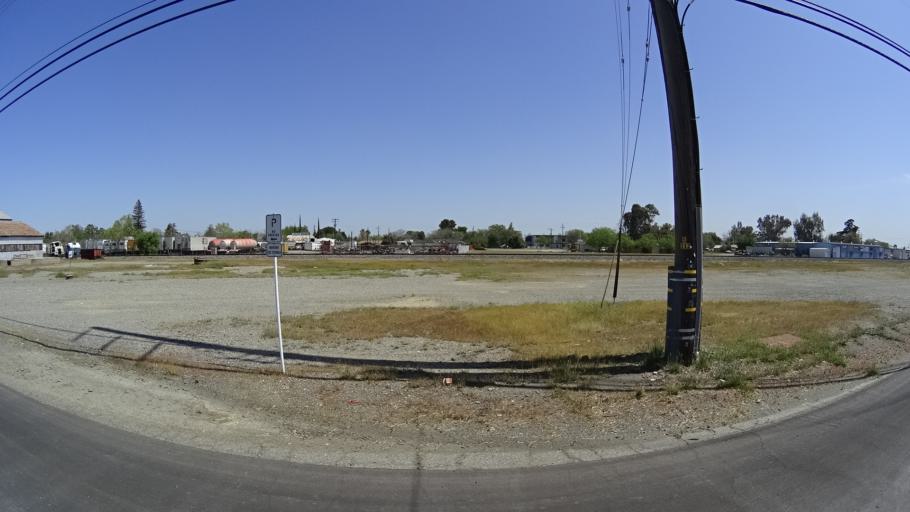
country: US
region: California
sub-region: Glenn County
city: Orland
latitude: 39.7421
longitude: -122.1977
